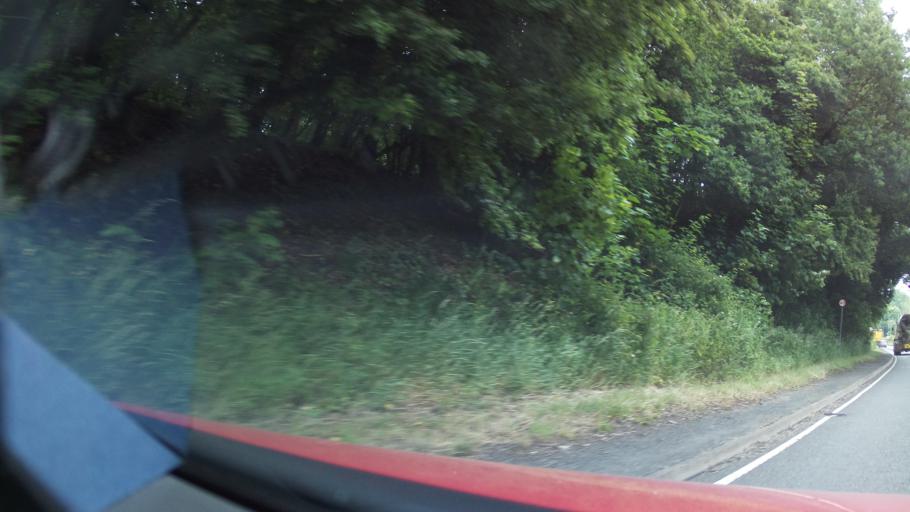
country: GB
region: England
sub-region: Leicestershire
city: Markfield
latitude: 52.6733
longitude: -1.2498
